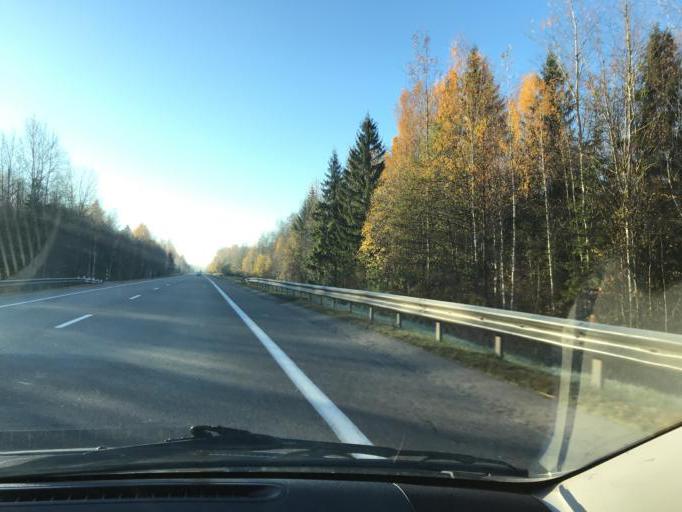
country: BY
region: Vitebsk
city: Vitebsk
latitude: 54.9857
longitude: 30.3439
